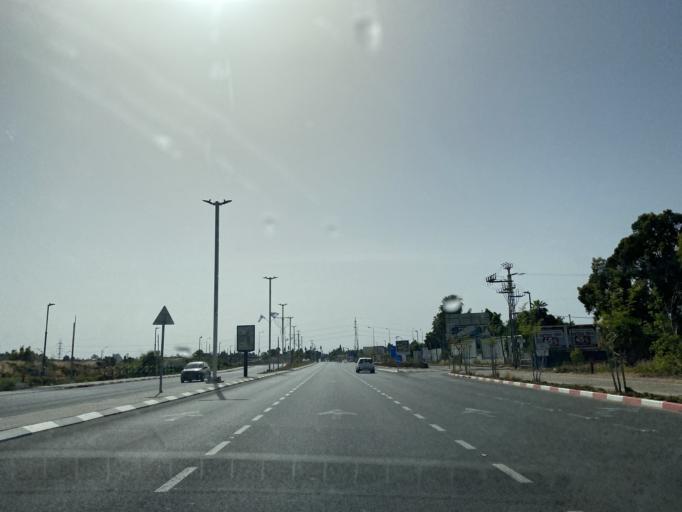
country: IL
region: Tel Aviv
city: Kefar Shemaryahu
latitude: 32.1786
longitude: 34.8291
